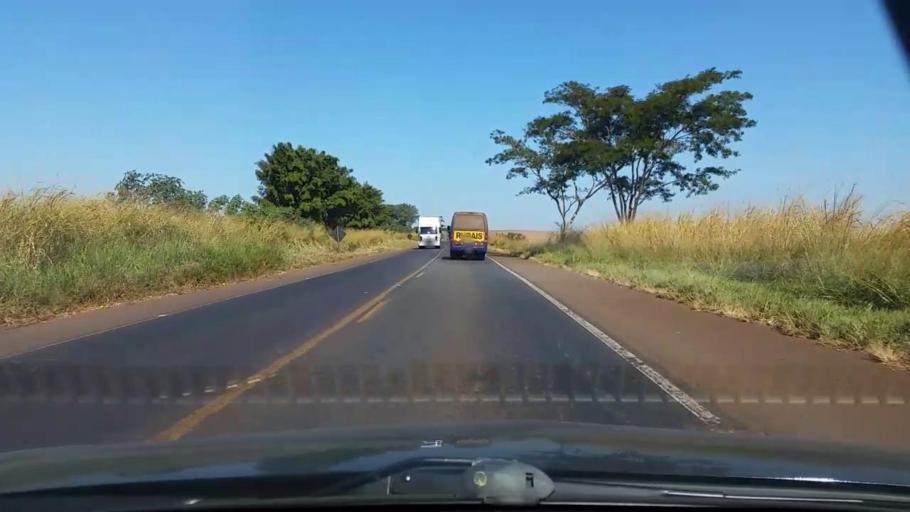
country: BR
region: Sao Paulo
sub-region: Igaracu Do Tiete
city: Igaracu do Tiete
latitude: -22.5658
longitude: -48.5638
